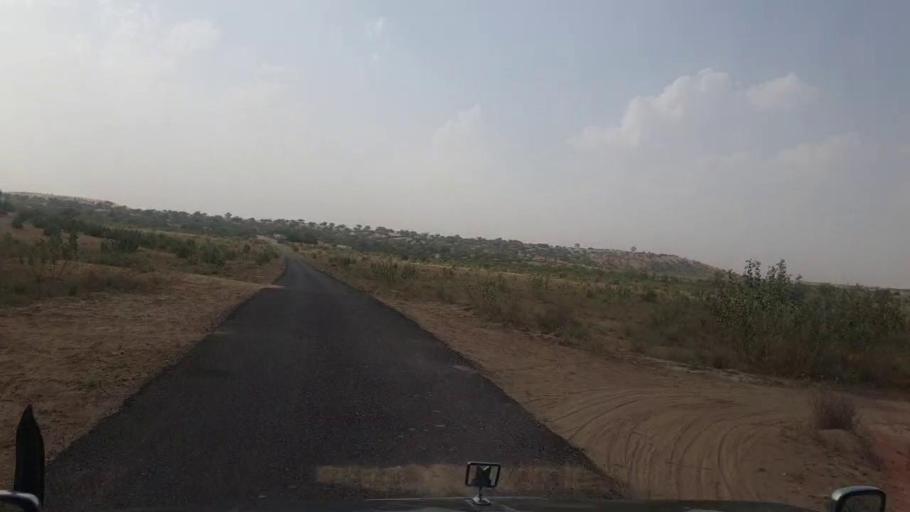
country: PK
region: Sindh
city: Islamkot
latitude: 25.2300
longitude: 70.2797
